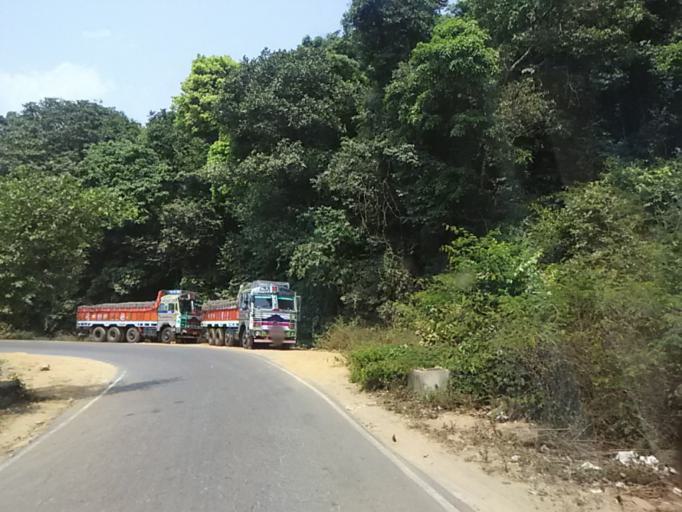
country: IN
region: Karnataka
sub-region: Kodagu
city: Virarajendrapet
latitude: 12.1420
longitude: 75.7946
